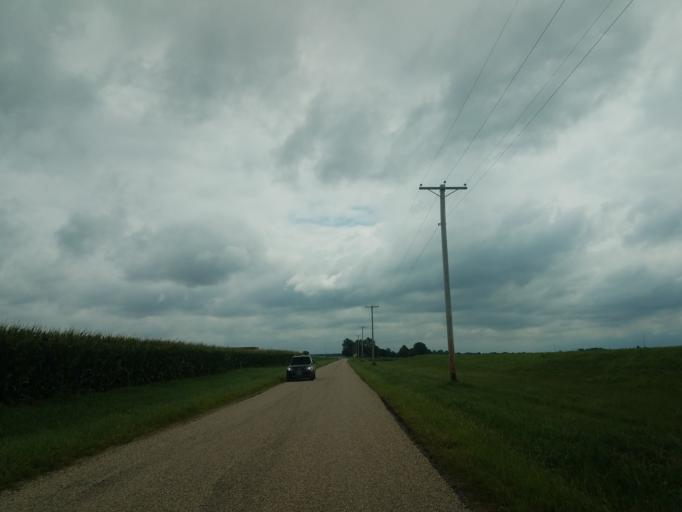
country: US
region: Illinois
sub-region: McLean County
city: Twin Grove
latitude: 40.4368
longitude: -89.0594
